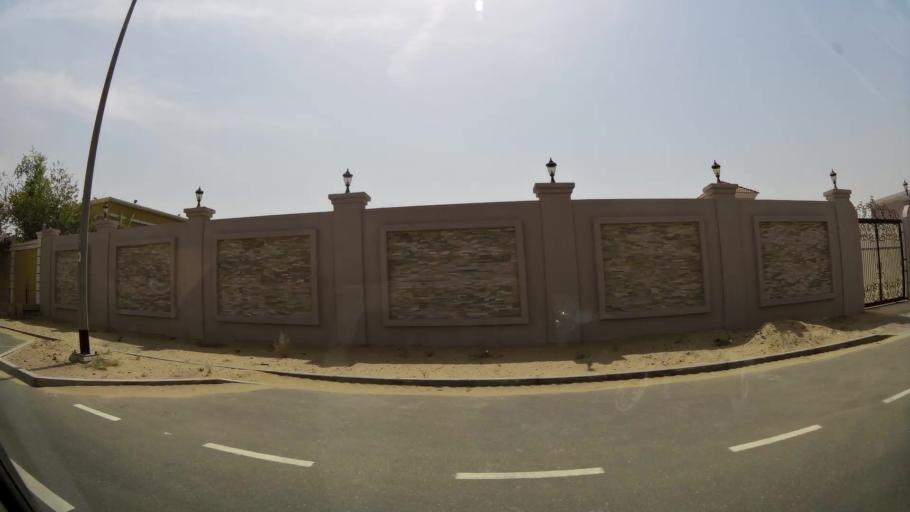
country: AE
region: Ash Shariqah
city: Sharjah
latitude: 25.2499
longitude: 55.4869
